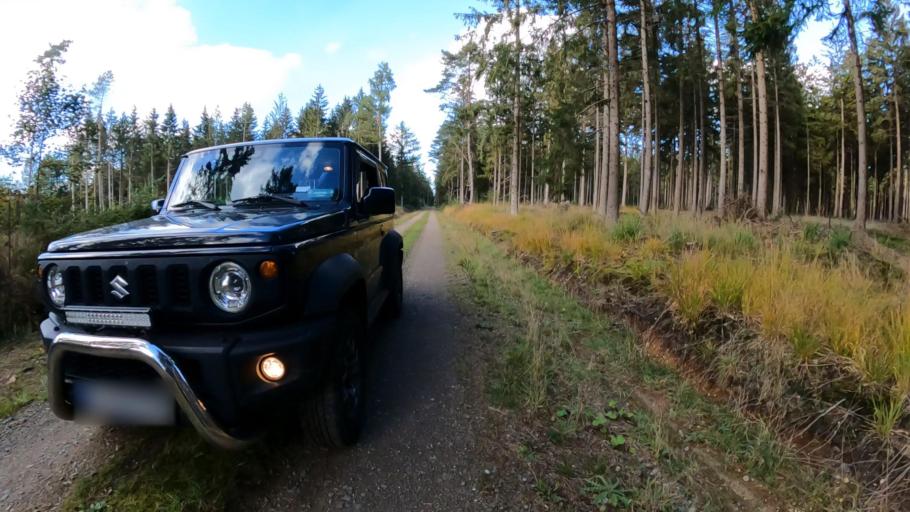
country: DE
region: Schleswig-Holstein
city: Hartenholm
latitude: 53.9221
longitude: 10.0801
